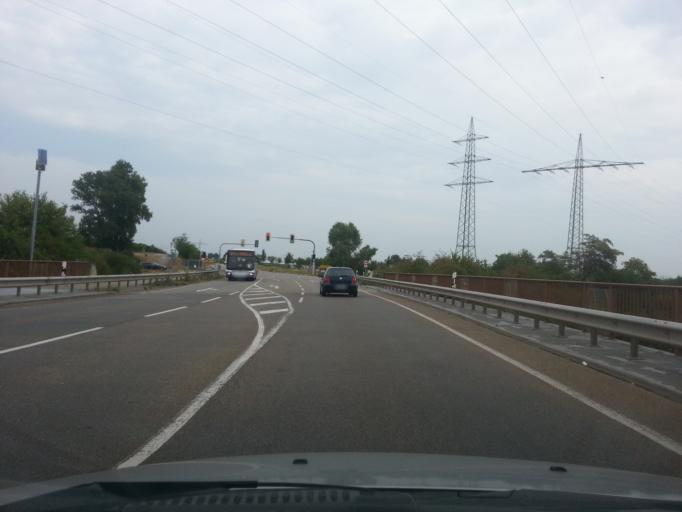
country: DE
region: Rheinland-Pfalz
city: Landau in der Pfalz
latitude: 49.2155
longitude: 8.1290
